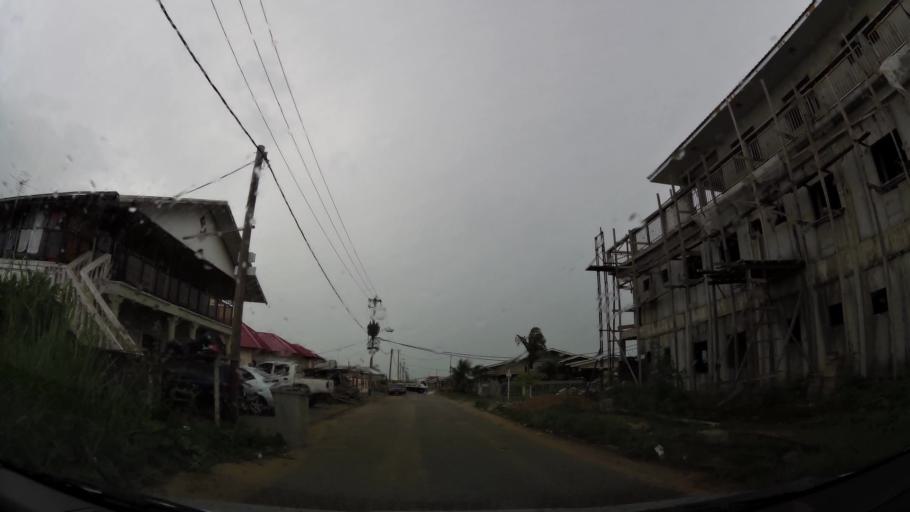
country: SR
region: Commewijne
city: Nieuw Amsterdam
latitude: 5.8561
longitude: -55.1179
